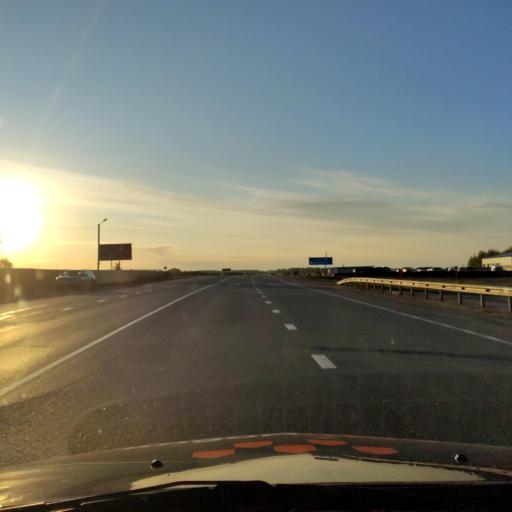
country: RU
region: Orjol
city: Livny
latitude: 52.4498
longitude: 37.5019
